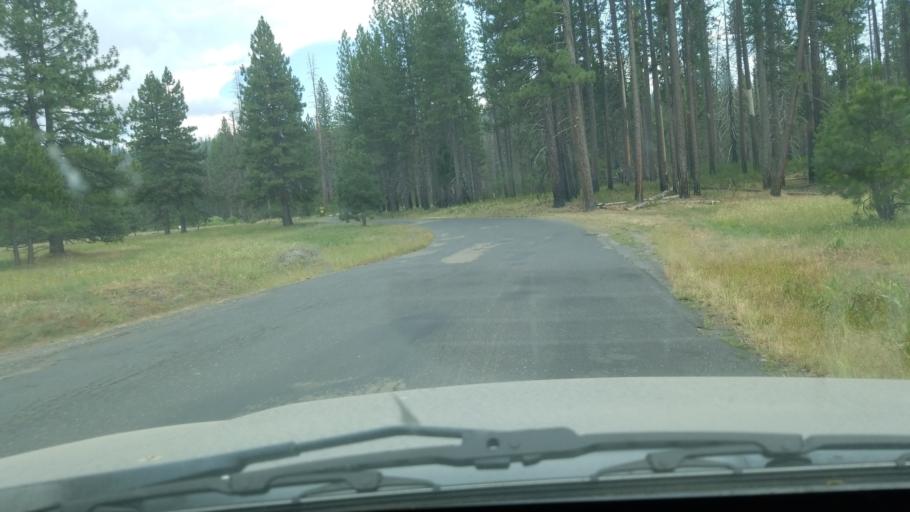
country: US
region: California
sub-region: Mariposa County
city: Yosemite Valley
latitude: 37.8367
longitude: -119.8479
